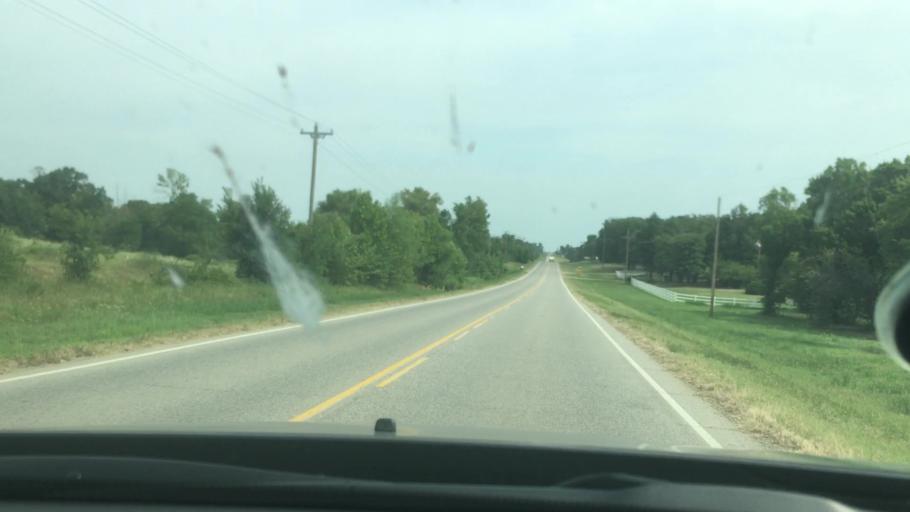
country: US
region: Oklahoma
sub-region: Johnston County
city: Tishomingo
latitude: 34.2542
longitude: -96.4248
